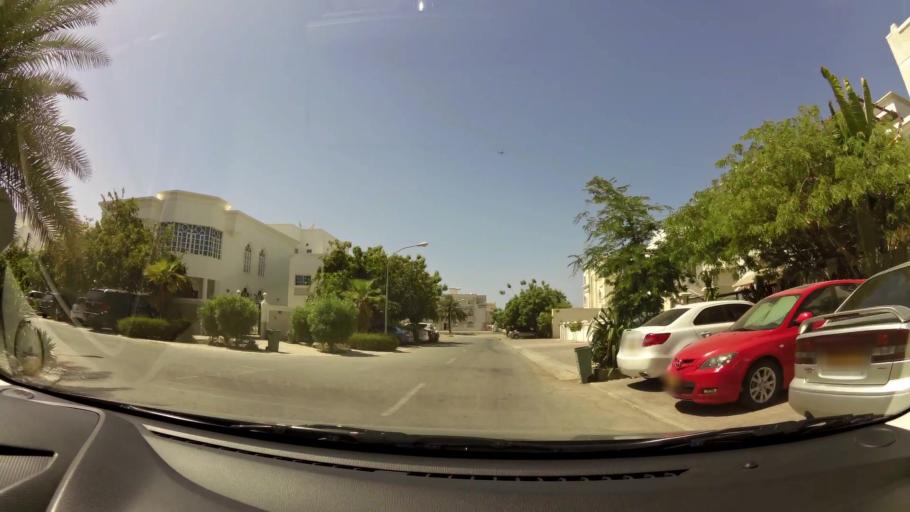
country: OM
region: Muhafazat Masqat
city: Bawshar
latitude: 23.6013
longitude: 58.3608
